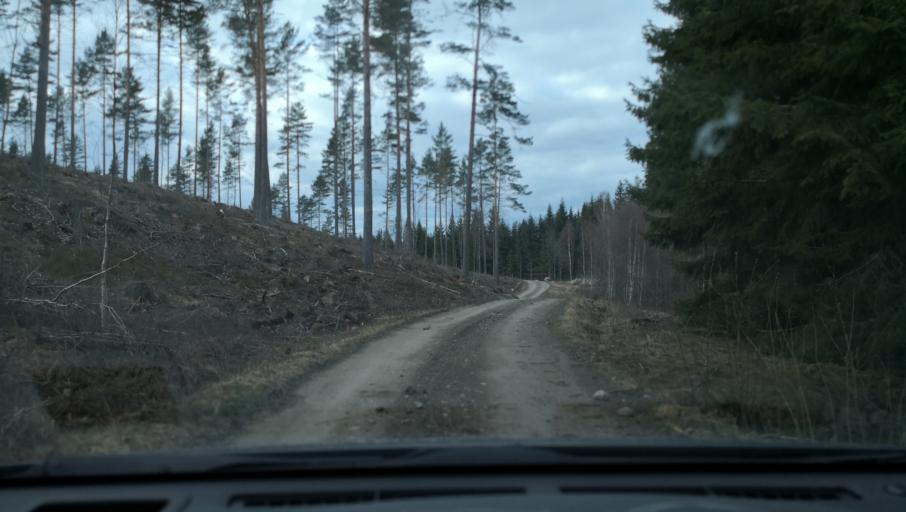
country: SE
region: Soedermanland
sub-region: Katrineholms Kommun
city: Katrineholm
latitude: 59.1295
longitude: 16.1572
